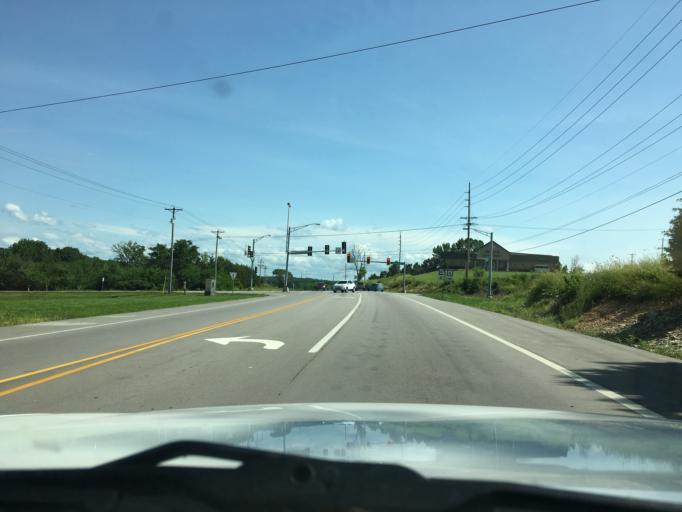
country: US
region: Missouri
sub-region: Franklin County
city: Union
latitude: 38.4610
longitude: -91.0049
